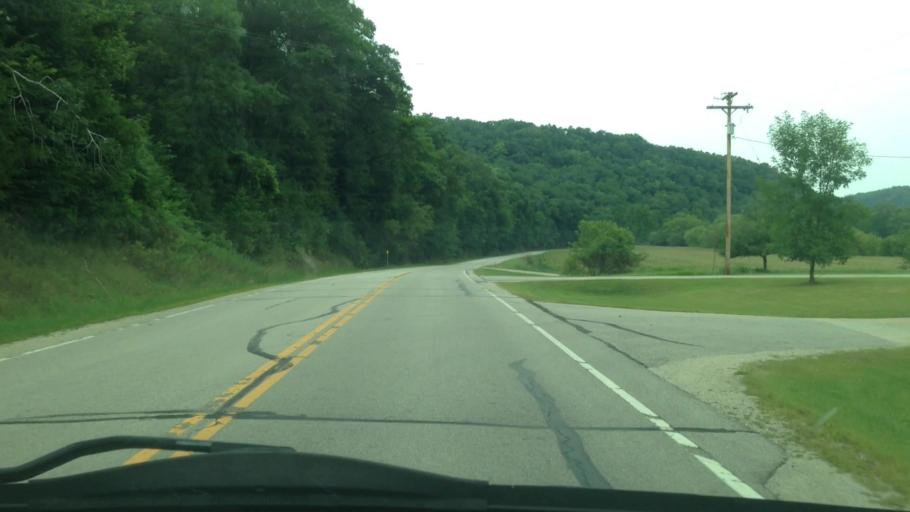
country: US
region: Minnesota
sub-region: Fillmore County
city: Preston
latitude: 43.7270
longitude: -91.9639
